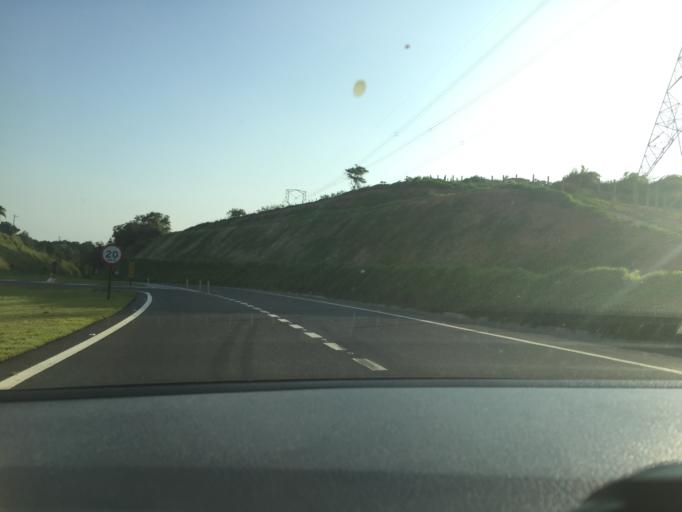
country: BR
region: Sao Paulo
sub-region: Louveira
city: Louveira
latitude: -23.0750
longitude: -46.9077
